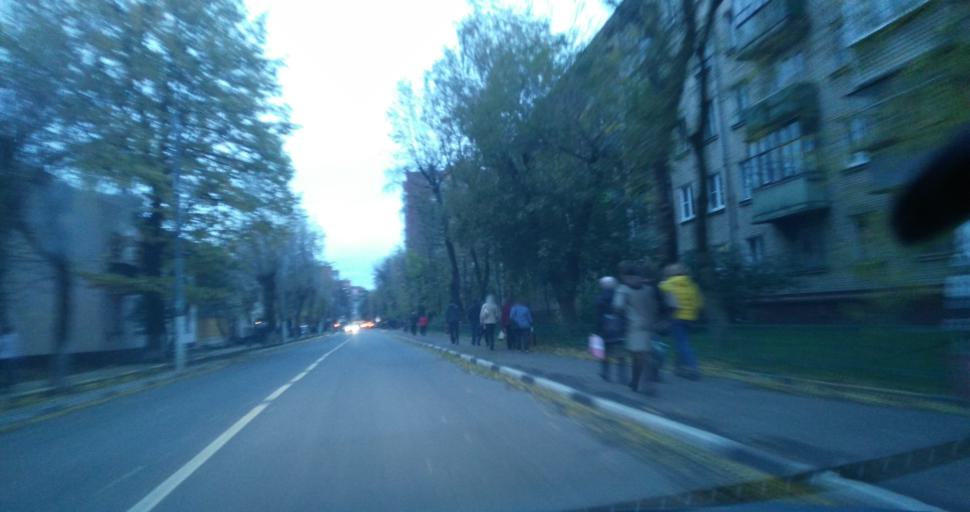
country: RU
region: Moscow
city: Khimki
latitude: 55.8955
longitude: 37.4371
